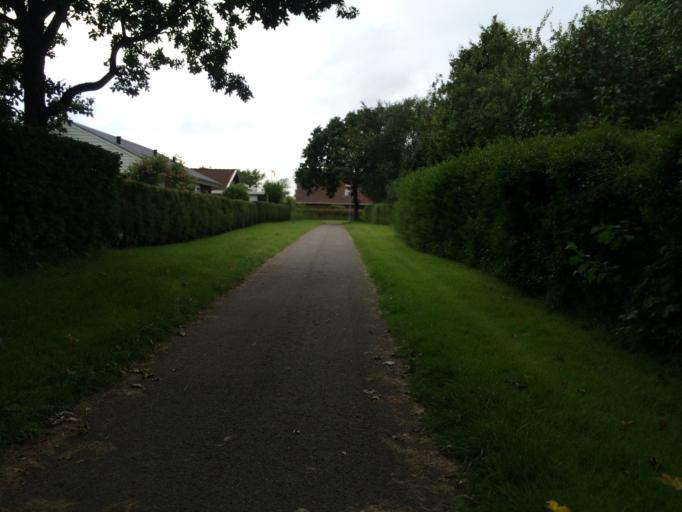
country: DK
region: Central Jutland
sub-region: Holstebro Kommune
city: Ulfborg
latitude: 56.2745
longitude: 8.3129
